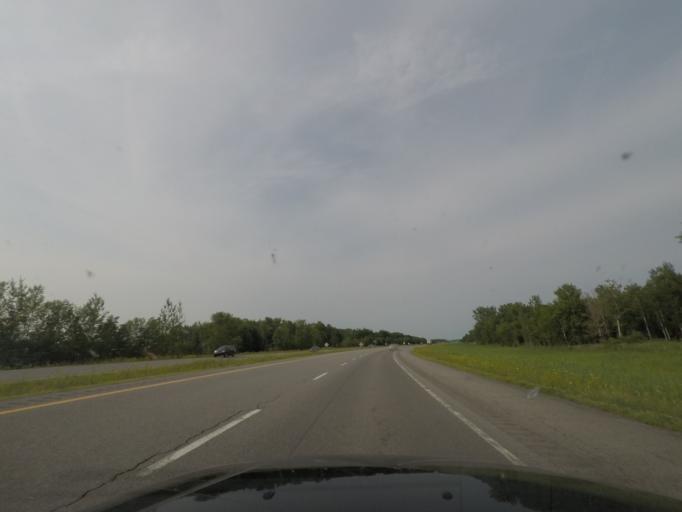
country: CA
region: Quebec
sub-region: Monteregie
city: Napierville
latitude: 45.1634
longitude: -73.4674
